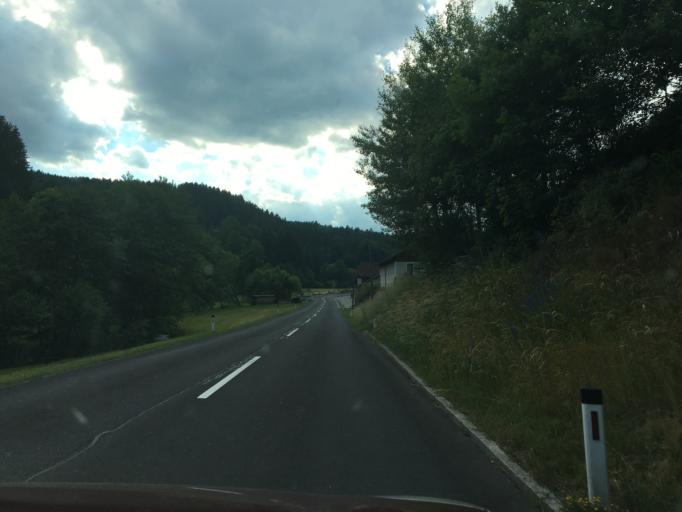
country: AT
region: Upper Austria
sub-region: Politischer Bezirk Urfahr-Umgebung
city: Alberndorf in der Riedmark
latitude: 48.4241
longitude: 14.3885
